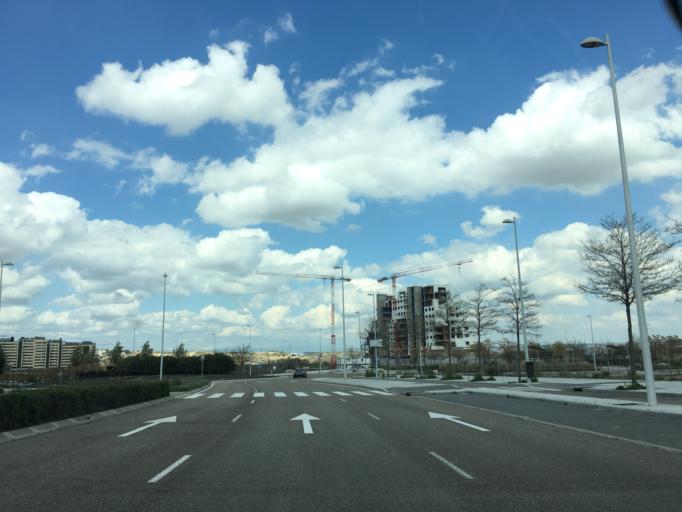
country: ES
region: Madrid
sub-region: Provincia de Madrid
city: Hortaleza
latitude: 40.4902
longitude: -3.6106
